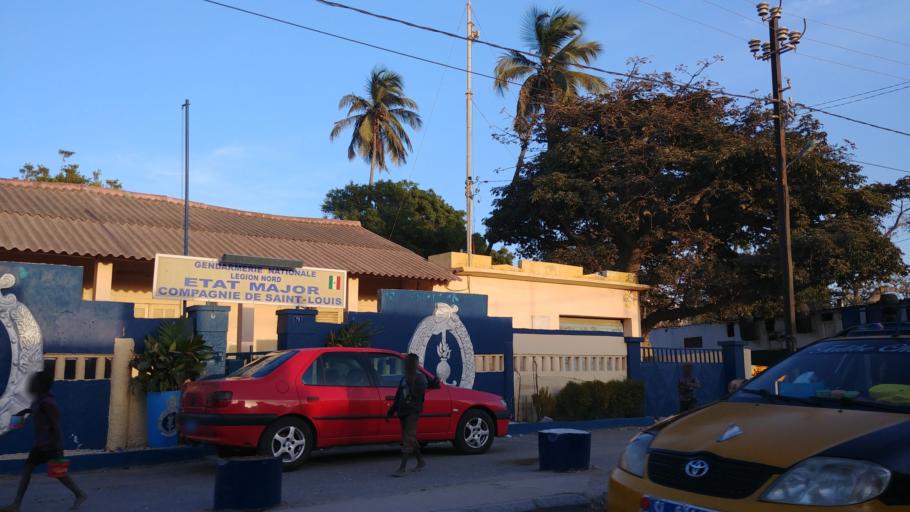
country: SN
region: Saint-Louis
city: Saint-Louis
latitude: 16.0221
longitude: -16.4914
